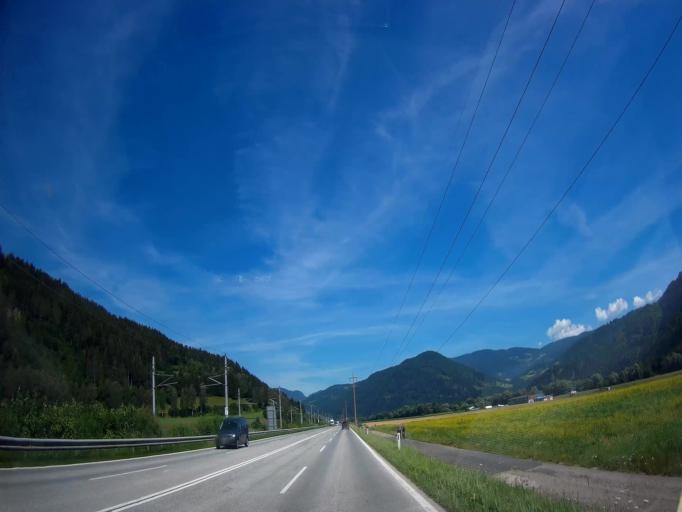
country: AT
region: Carinthia
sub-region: Politischer Bezirk Sankt Veit an der Glan
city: Micheldorf
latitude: 46.9235
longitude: 14.4293
